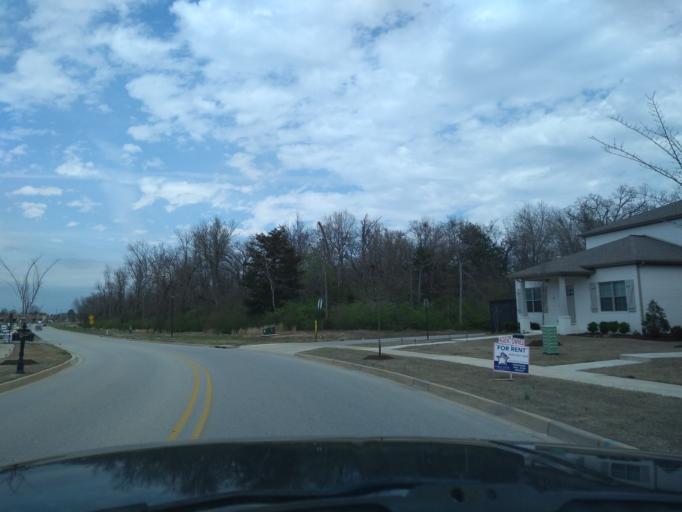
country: US
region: Arkansas
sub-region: Washington County
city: Farmington
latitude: 36.0722
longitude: -94.2090
